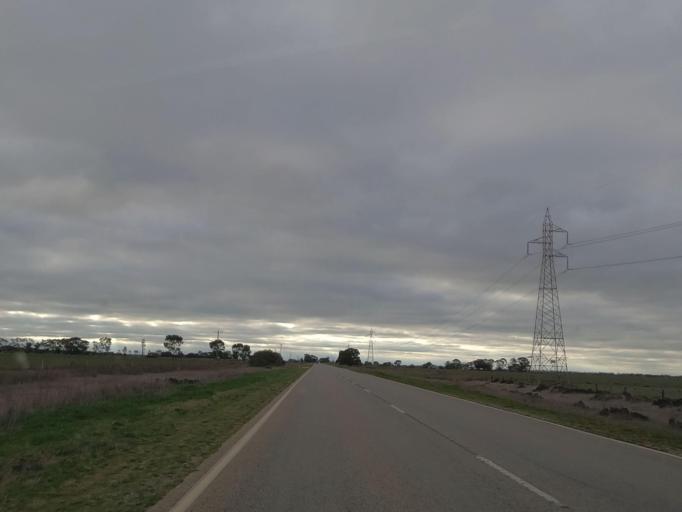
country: AU
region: Victoria
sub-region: Swan Hill
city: Swan Hill
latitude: -35.8911
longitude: 143.9430
